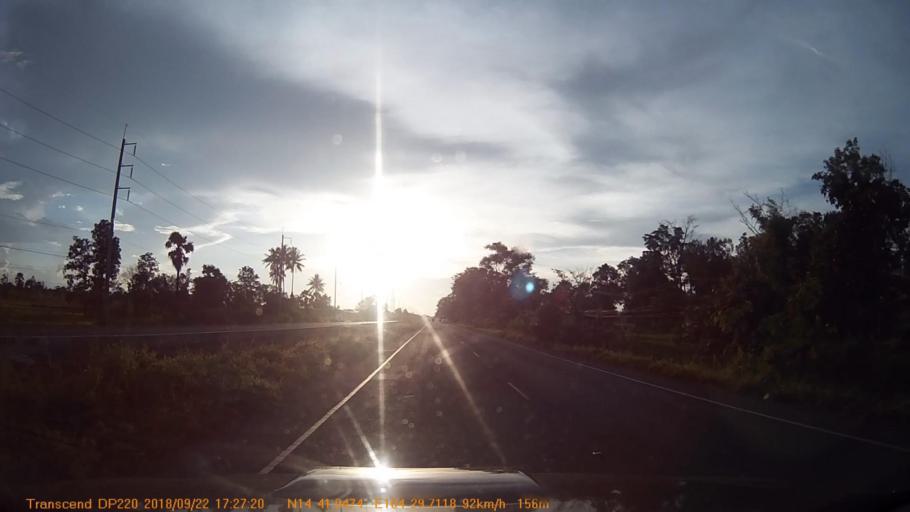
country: TH
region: Sisaket
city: Khun Han
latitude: 14.6845
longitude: 104.4951
